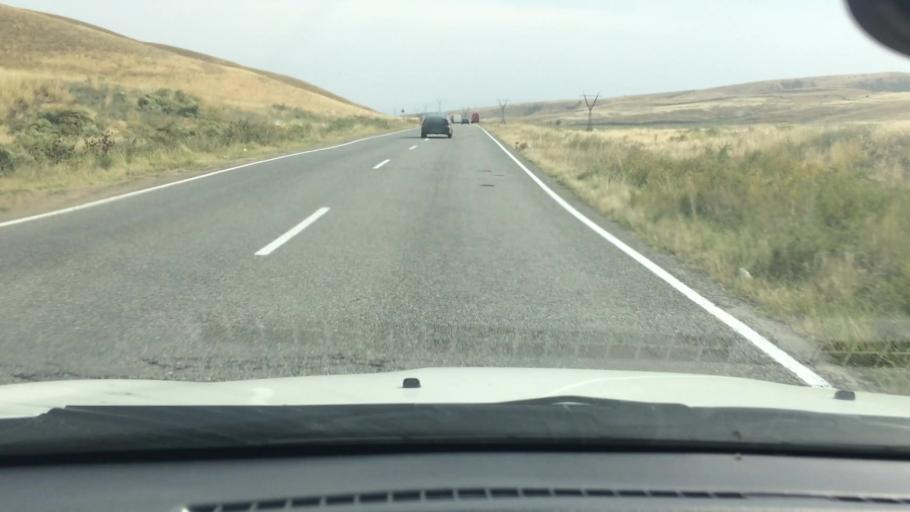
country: GE
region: Kvemo Kartli
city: Rust'avi
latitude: 41.5044
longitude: 44.9540
